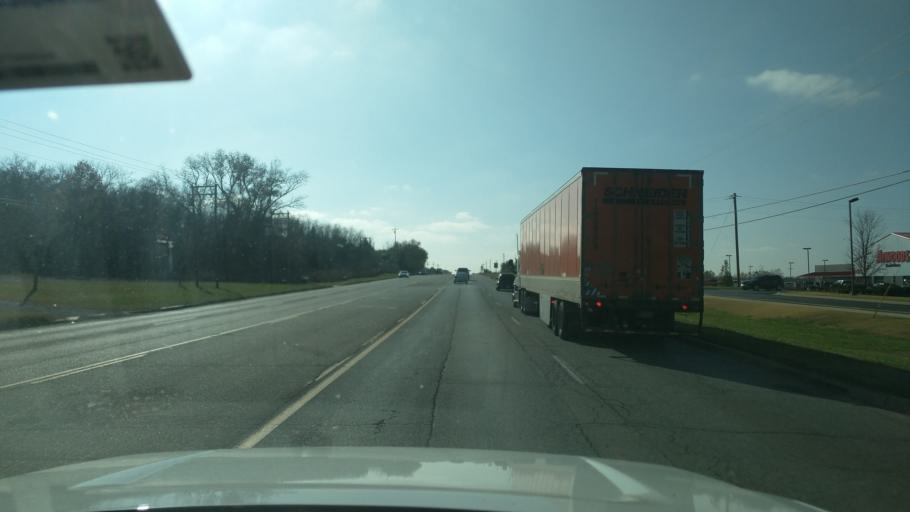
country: US
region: Oklahoma
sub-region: Washington County
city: Bartlesville
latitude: 36.7053
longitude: -95.9352
